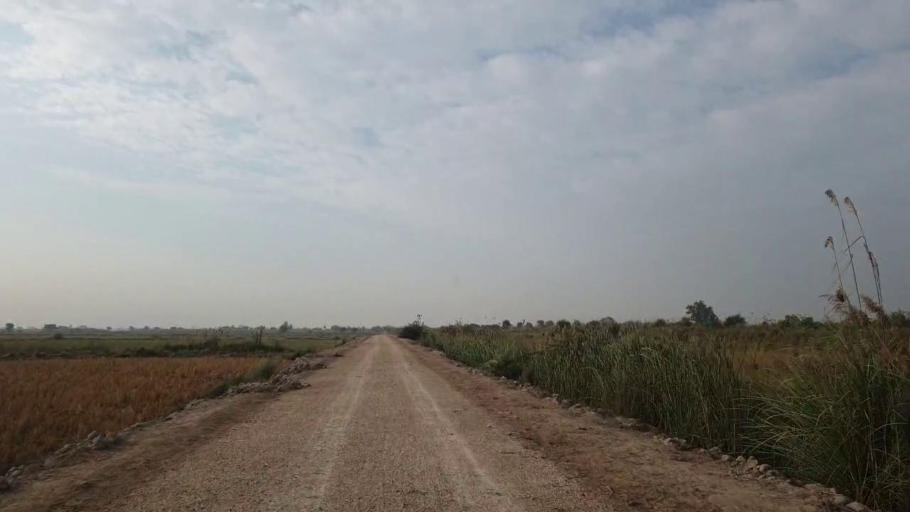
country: PK
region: Sindh
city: Tando Muhammad Khan
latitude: 25.1087
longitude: 68.4236
